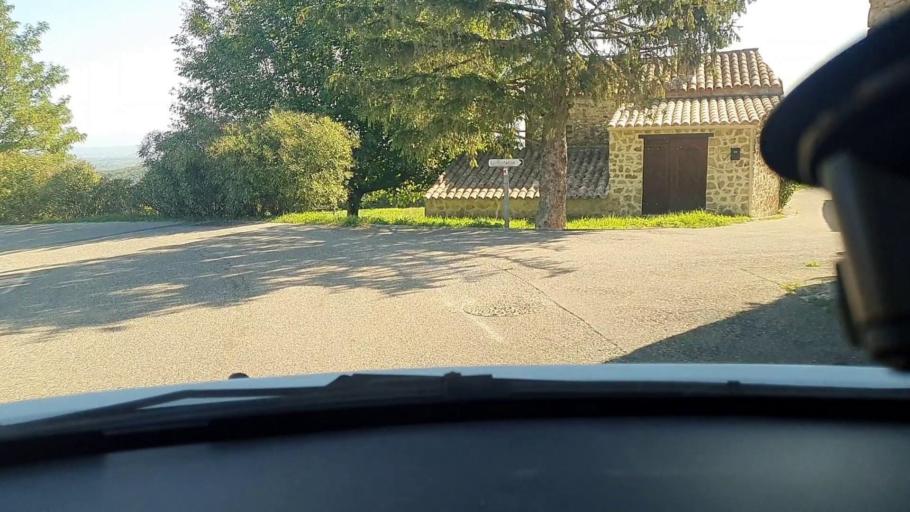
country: FR
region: Languedoc-Roussillon
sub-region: Departement du Gard
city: Saint-Julien-de-Peyrolas
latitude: 44.2610
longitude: 4.5254
